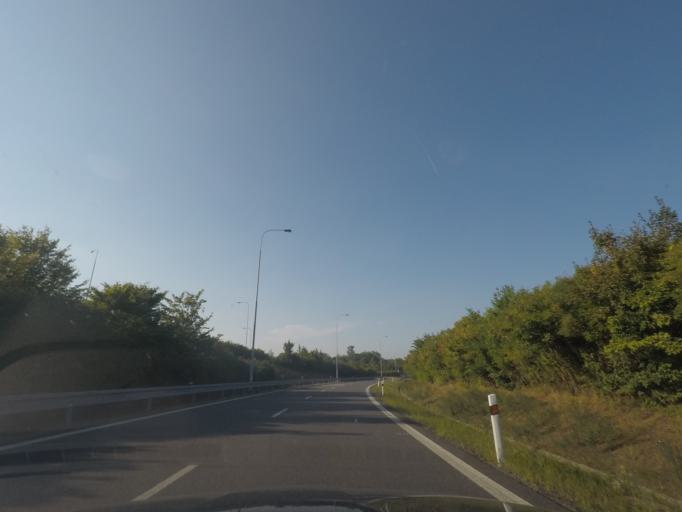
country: CZ
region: Olomoucky
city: Hnevotin
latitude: 49.5693
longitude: 17.2171
